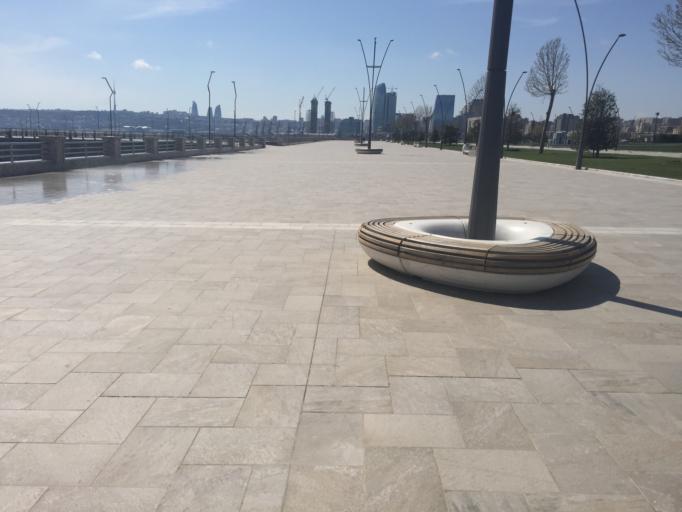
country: AZ
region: Baki
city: Baku
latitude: 40.3743
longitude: 49.8834
